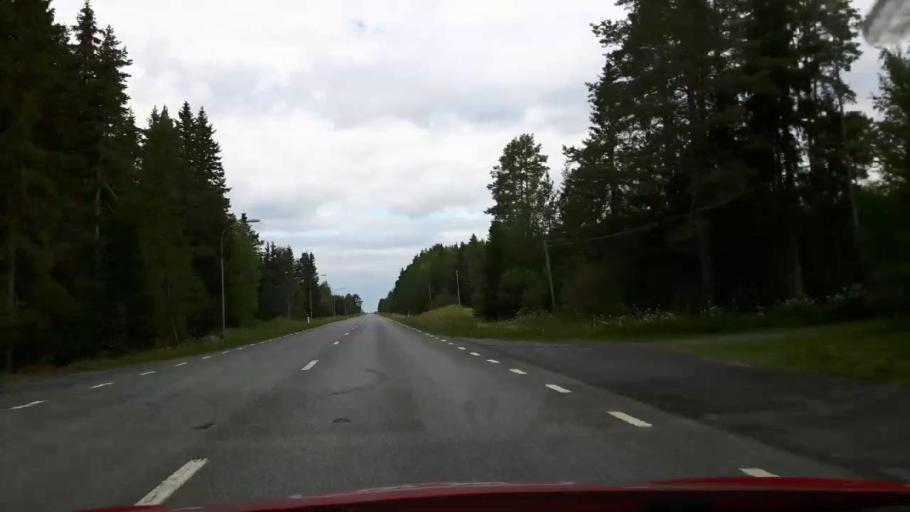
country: SE
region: Jaemtland
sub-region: Stroemsunds Kommun
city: Stroemsund
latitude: 63.5607
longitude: 15.3698
